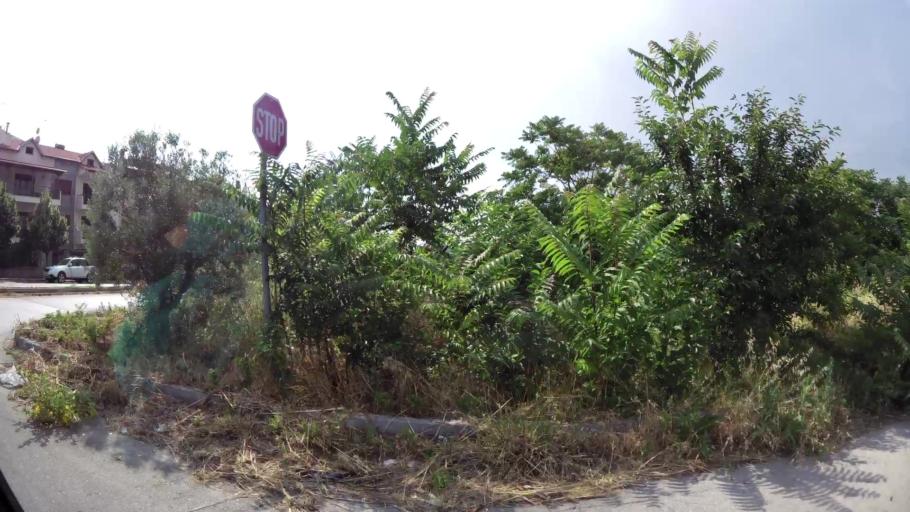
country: GR
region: Central Macedonia
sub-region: Nomos Thessalonikis
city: Polichni
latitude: 40.6681
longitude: 22.9538
